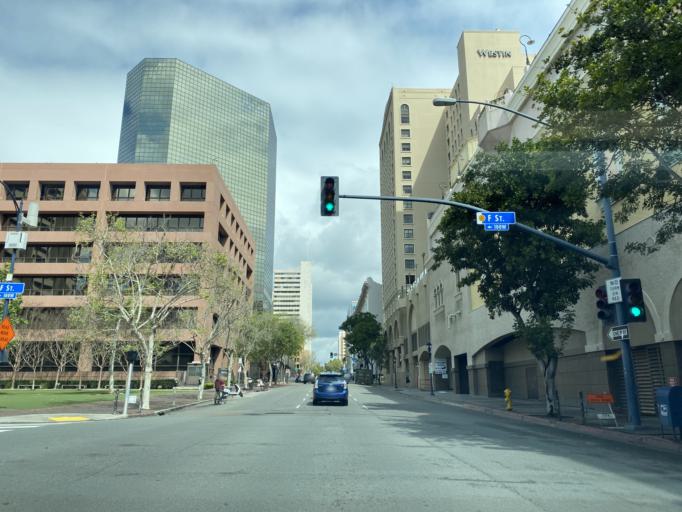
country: US
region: California
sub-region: San Diego County
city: San Diego
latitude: 32.7134
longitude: -117.1637
